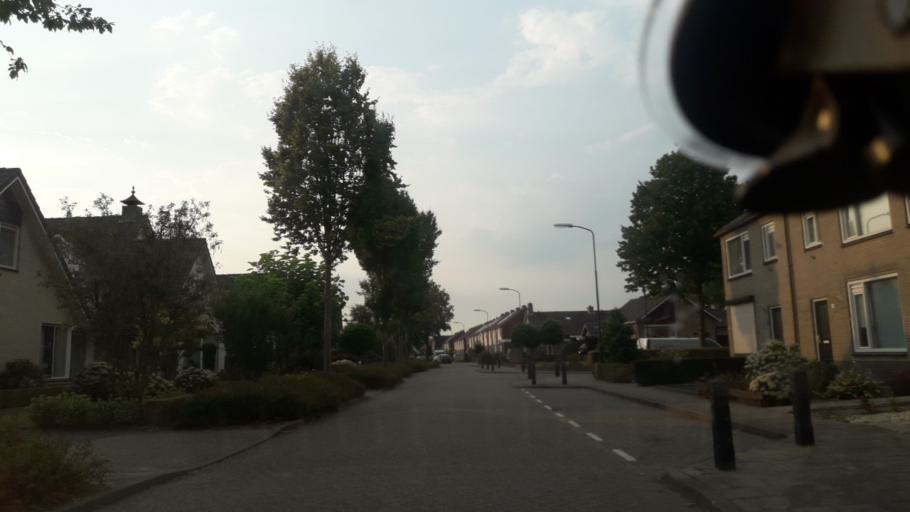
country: NL
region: Gelderland
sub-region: Oude IJsselstreek
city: Varsseveld
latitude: 51.9379
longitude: 6.4533
